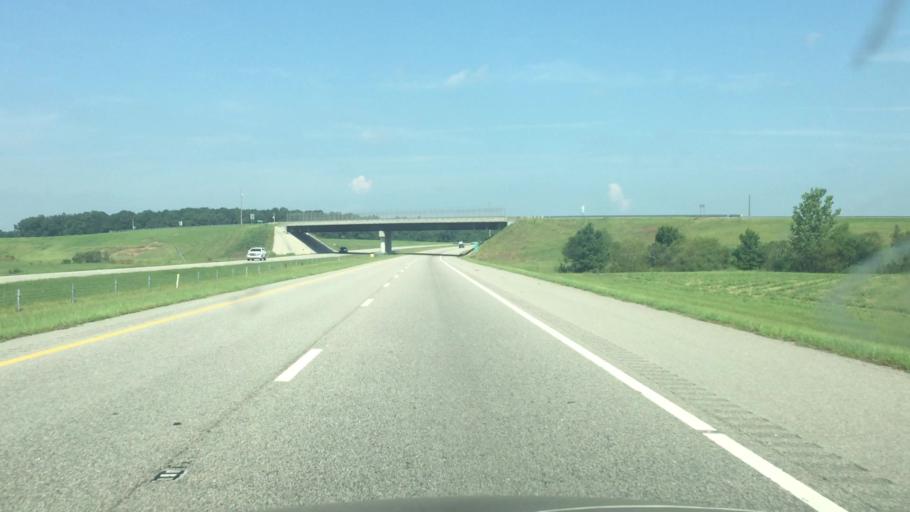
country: US
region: North Carolina
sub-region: Robeson County
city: Pembroke
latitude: 34.6033
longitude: -79.1980
